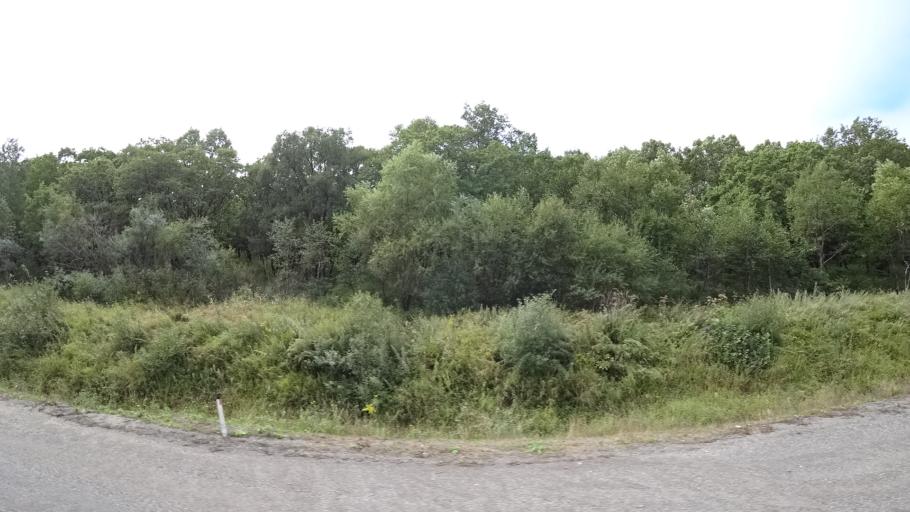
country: RU
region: Primorskiy
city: Lyalichi
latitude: 44.1015
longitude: 132.4241
